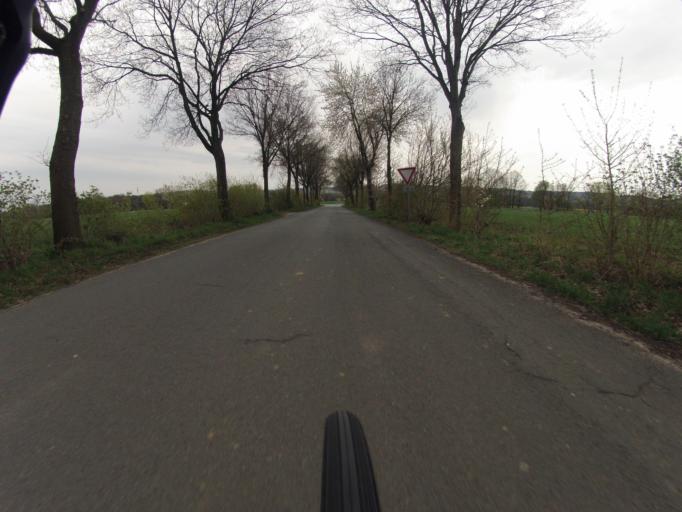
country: DE
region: North Rhine-Westphalia
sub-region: Regierungsbezirk Munster
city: Tecklenburg
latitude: 52.2508
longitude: 7.7872
